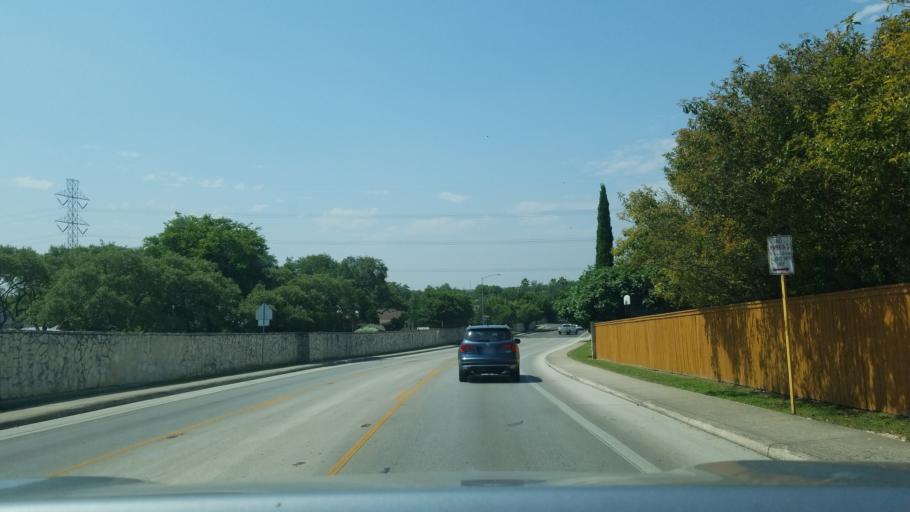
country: US
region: Texas
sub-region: Bexar County
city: Hollywood Park
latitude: 29.6344
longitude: -98.4445
